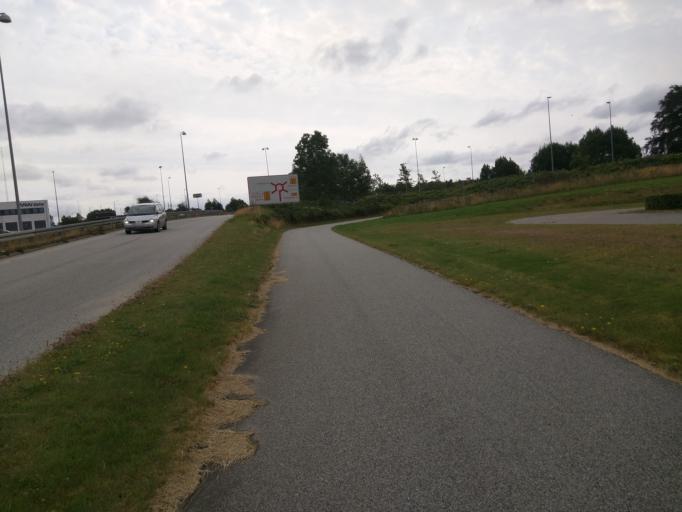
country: DK
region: Central Jutland
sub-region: Viborg Kommune
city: Viborg
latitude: 56.4485
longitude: 9.3687
